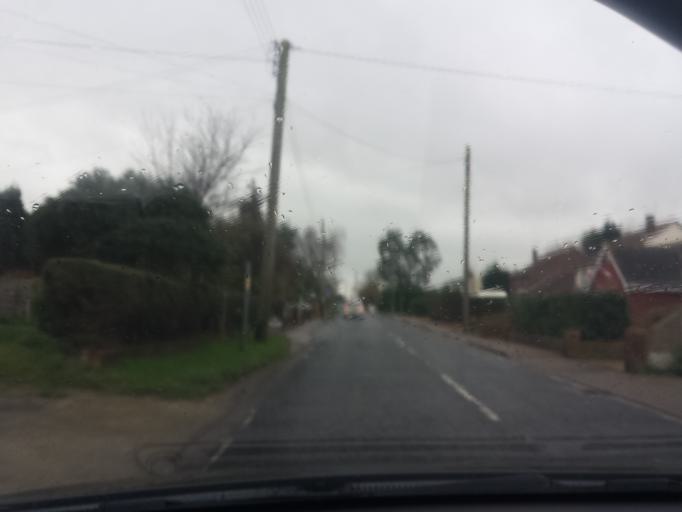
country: GB
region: England
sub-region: Essex
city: Dovercourt
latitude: 51.9180
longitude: 1.2276
